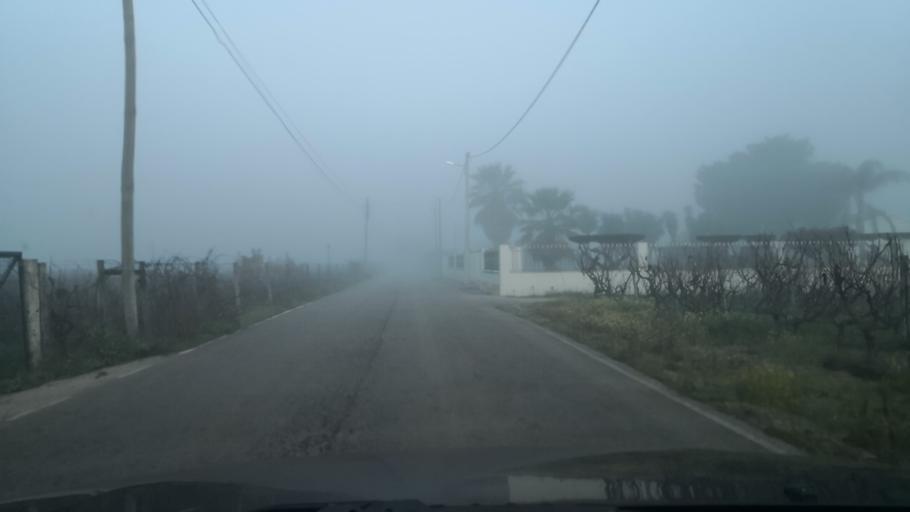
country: PT
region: Setubal
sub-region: Palmela
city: Palmela
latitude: 38.6043
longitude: -8.8498
